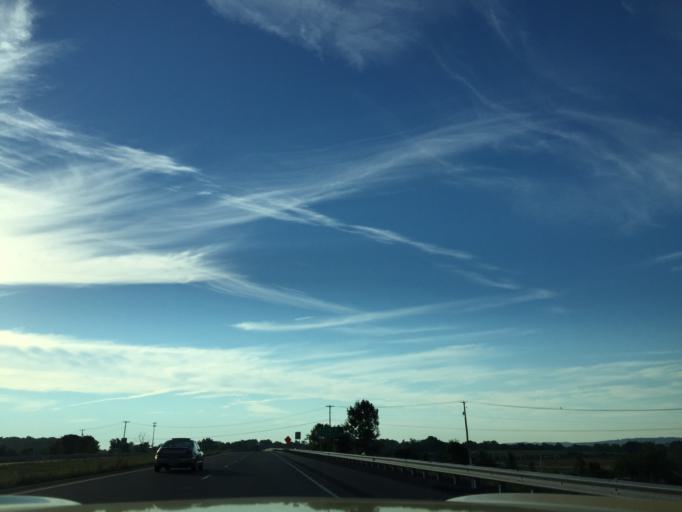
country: US
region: Pennsylvania
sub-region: Lehigh County
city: Ancient Oaks
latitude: 40.5645
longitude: -75.5891
